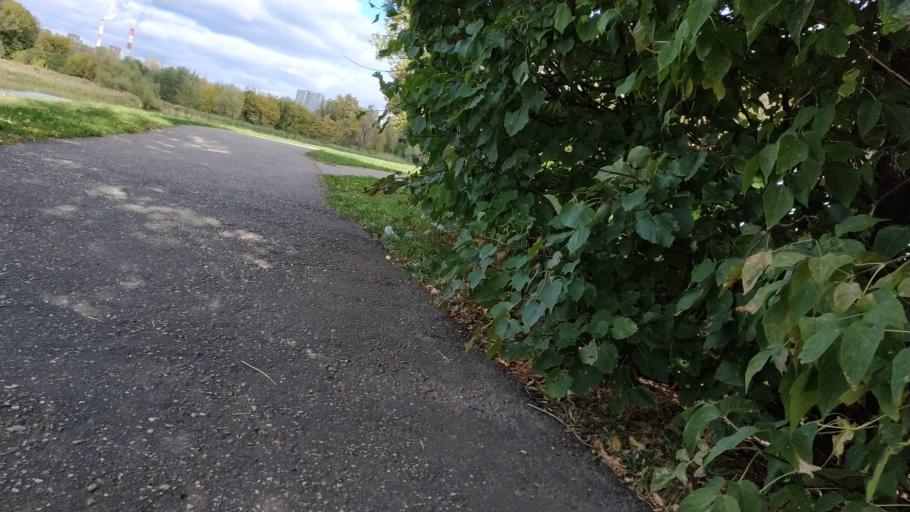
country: RU
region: Moscow
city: Metrogorodok
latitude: 55.7927
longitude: 37.7558
